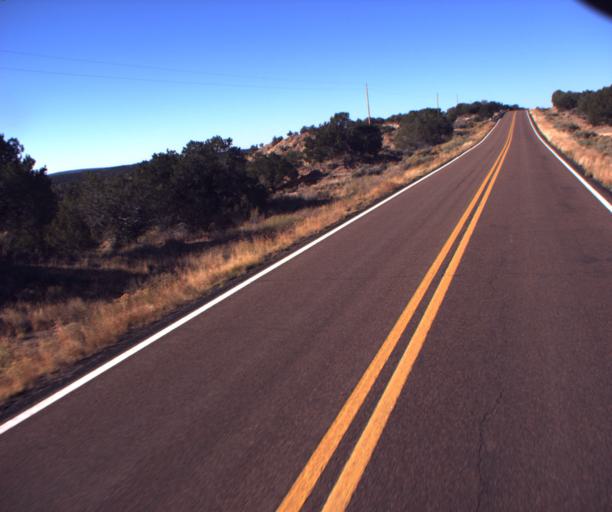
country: US
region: Arizona
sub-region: Apache County
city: Ganado
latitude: 35.7498
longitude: -109.9108
